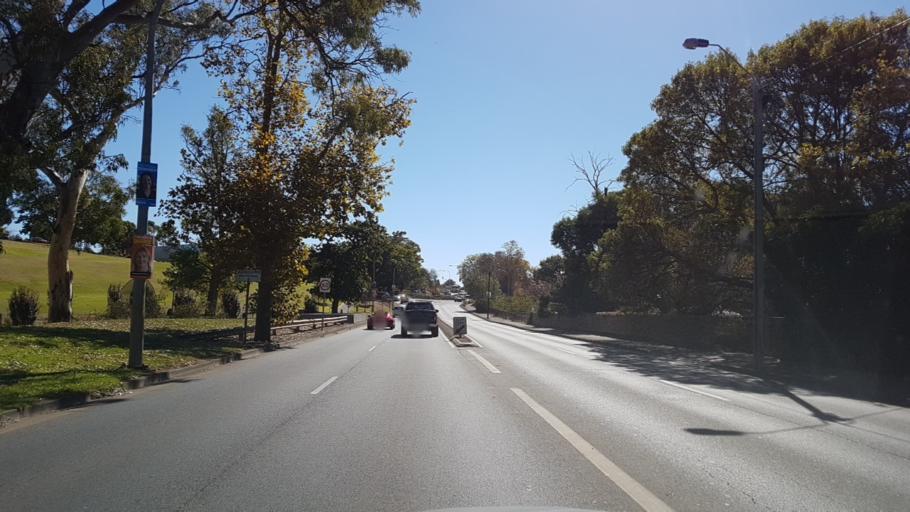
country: AU
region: South Australia
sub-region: Mount Barker
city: Mount Barker
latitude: -35.0709
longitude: 138.8572
